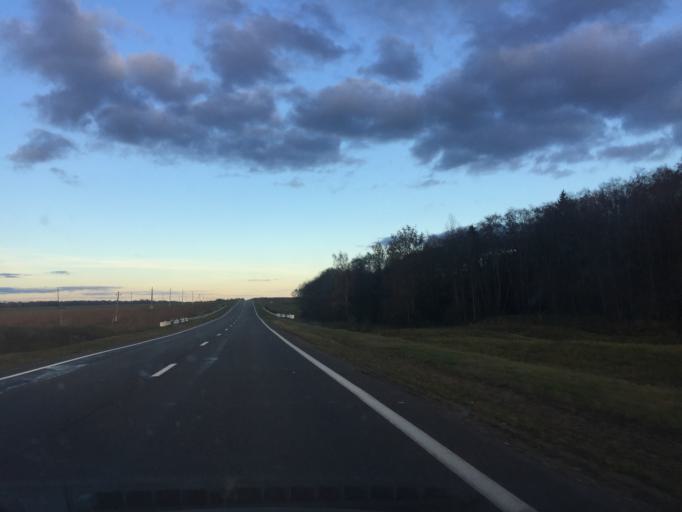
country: BY
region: Vitebsk
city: Vyerkhnyadzvinsk
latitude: 55.8227
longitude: 27.7453
